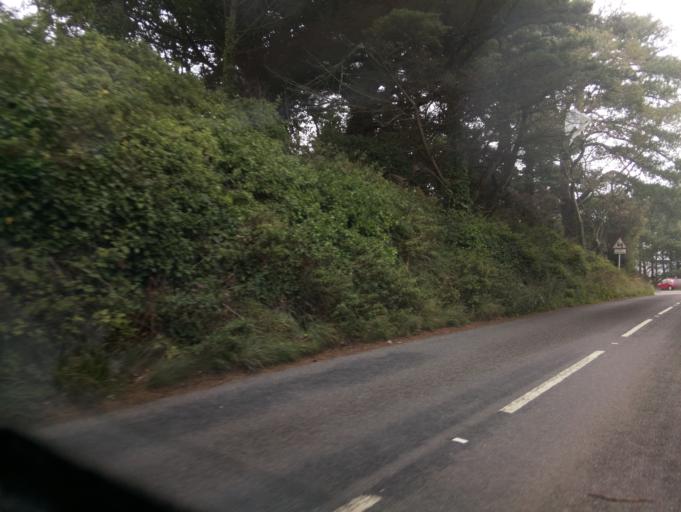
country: GB
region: England
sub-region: Devon
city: Dartmouth
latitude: 50.3153
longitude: -3.6172
